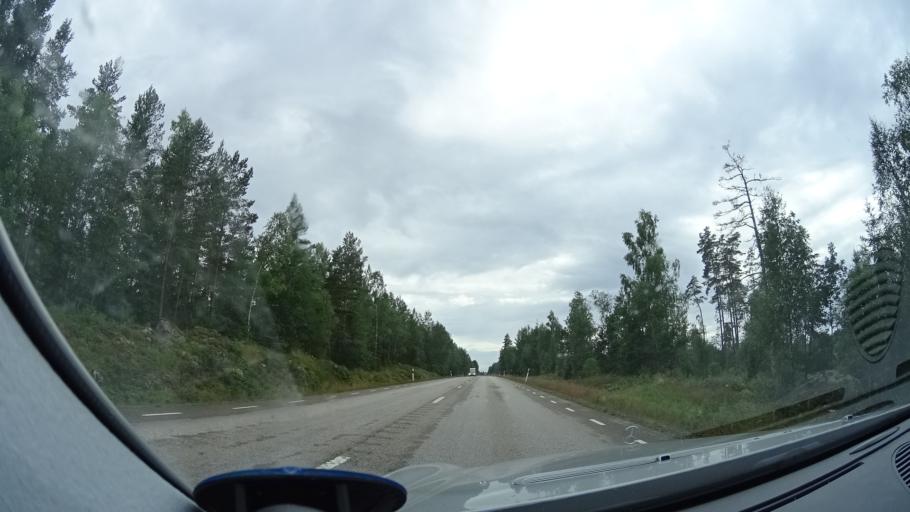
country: SE
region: Kronoberg
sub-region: Tingsryds Kommun
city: Tingsryd
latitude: 56.4252
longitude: 14.9596
